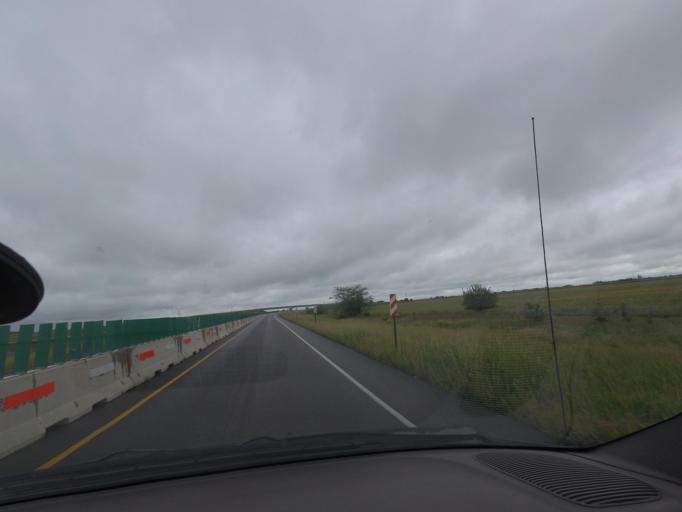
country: US
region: Illinois
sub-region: Piatt County
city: Cerro Gordo
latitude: 40.0081
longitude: -88.7742
